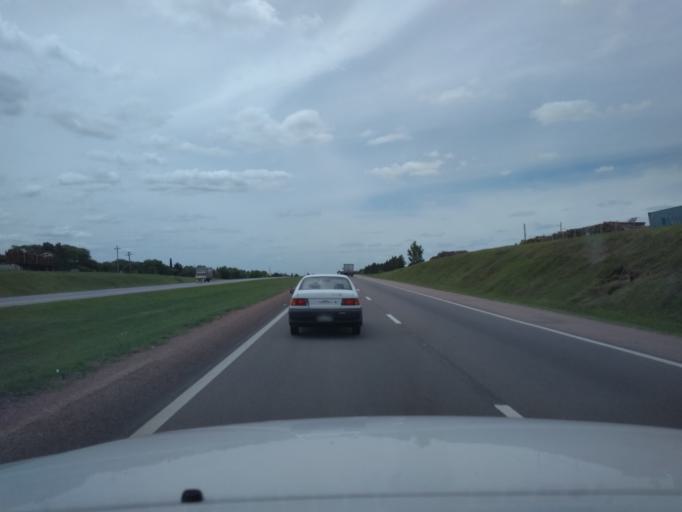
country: UY
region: Canelones
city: La Paz
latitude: -34.7431
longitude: -56.2520
